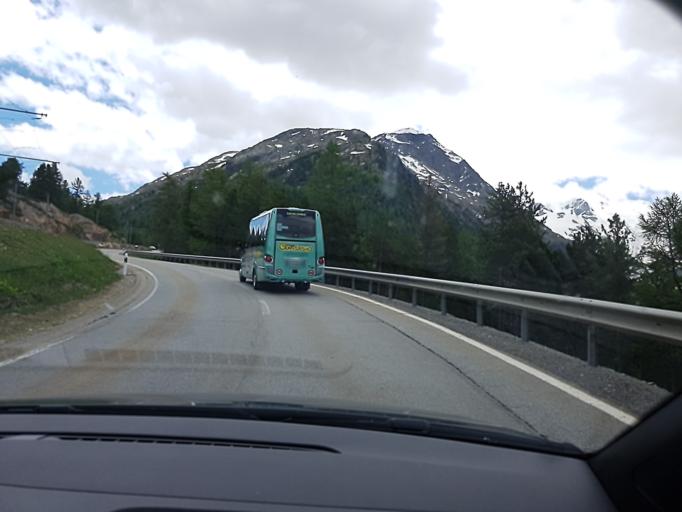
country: CH
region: Grisons
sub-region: Maloja District
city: Pontresina
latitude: 46.4555
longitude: 9.9448
